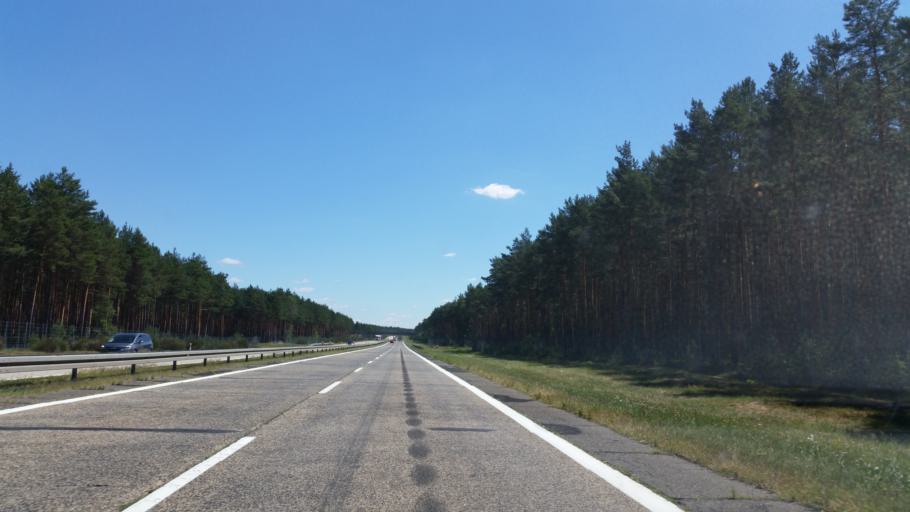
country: PL
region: Lubusz
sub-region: Powiat zaganski
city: Malomice
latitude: 51.4228
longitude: 15.4545
